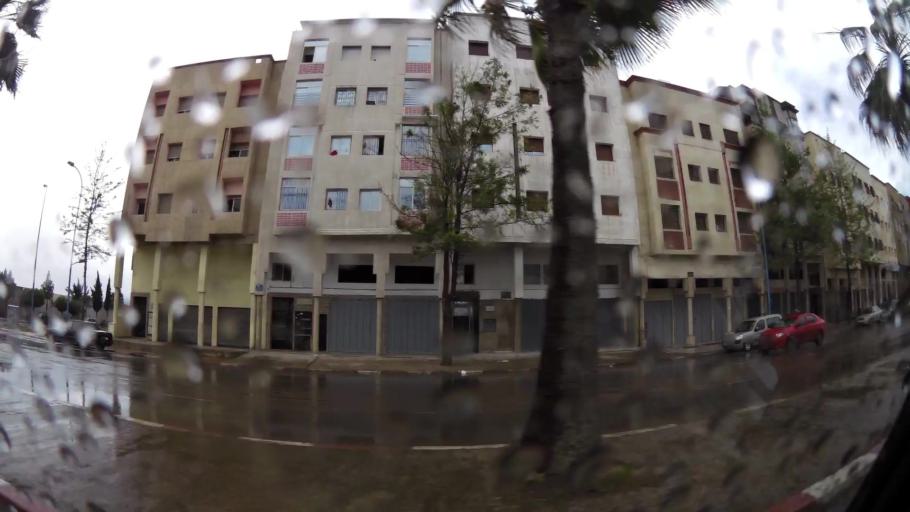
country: MA
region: Grand Casablanca
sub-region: Casablanca
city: Casablanca
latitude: 33.5475
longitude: -7.5561
